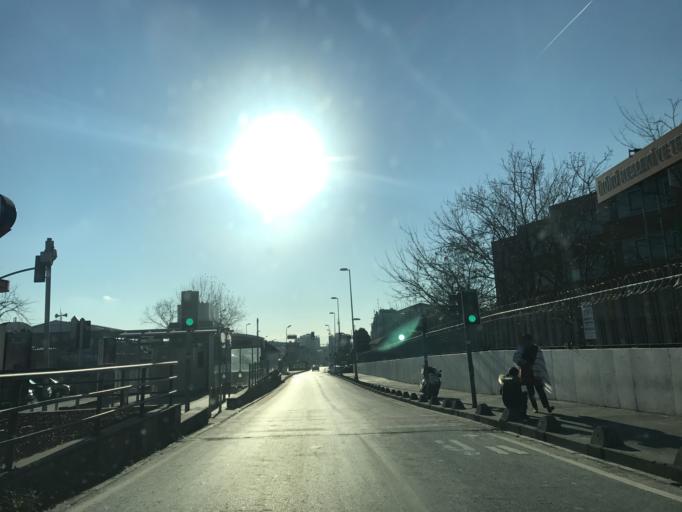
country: TR
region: Istanbul
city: Esenler
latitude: 41.0475
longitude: 28.9148
